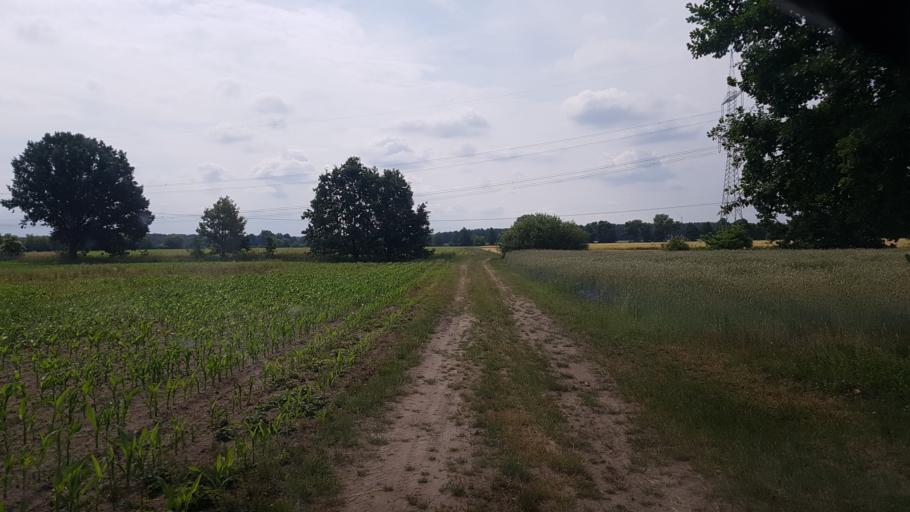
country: DE
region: Brandenburg
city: Schonewalde
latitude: 51.6545
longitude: 13.5934
